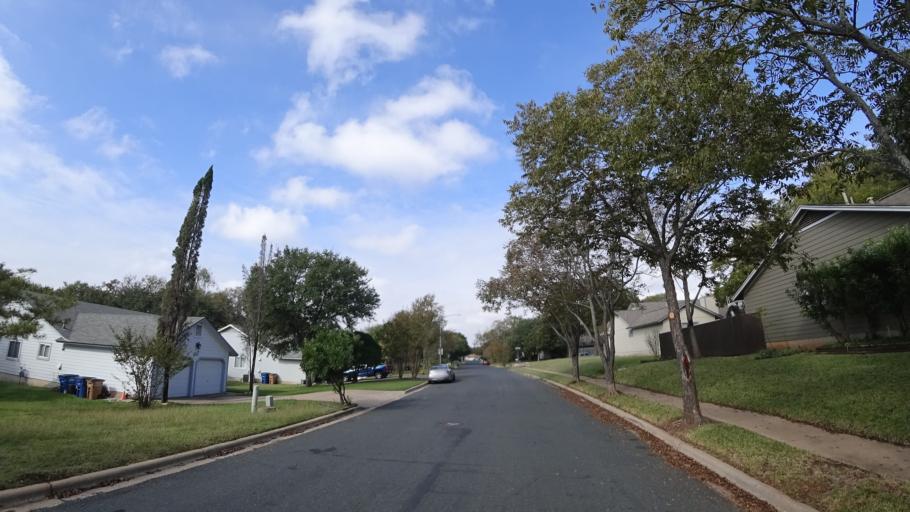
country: US
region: Texas
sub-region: Travis County
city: Wells Branch
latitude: 30.4286
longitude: -97.7263
